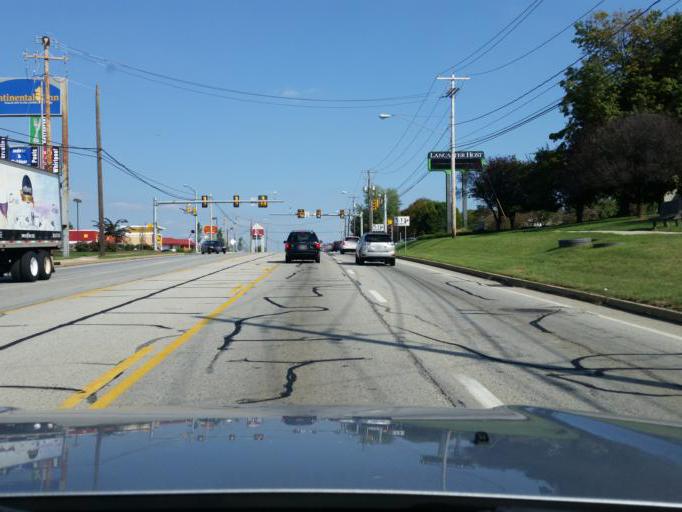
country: US
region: Pennsylvania
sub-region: Lancaster County
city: Lampeter
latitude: 40.0265
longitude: -76.2147
